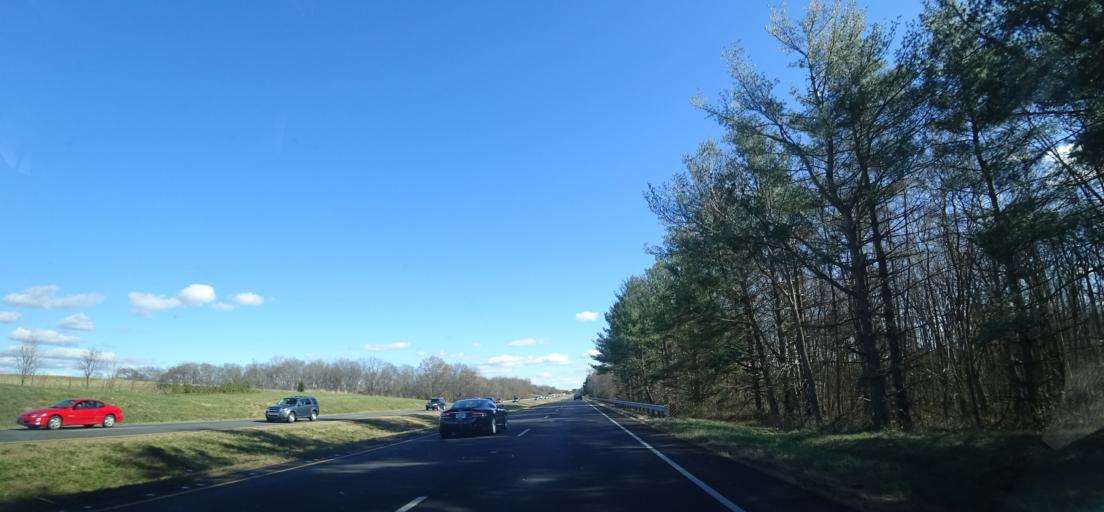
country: US
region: Virginia
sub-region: Culpeper County
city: Culpeper
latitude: 38.5001
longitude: -77.9154
